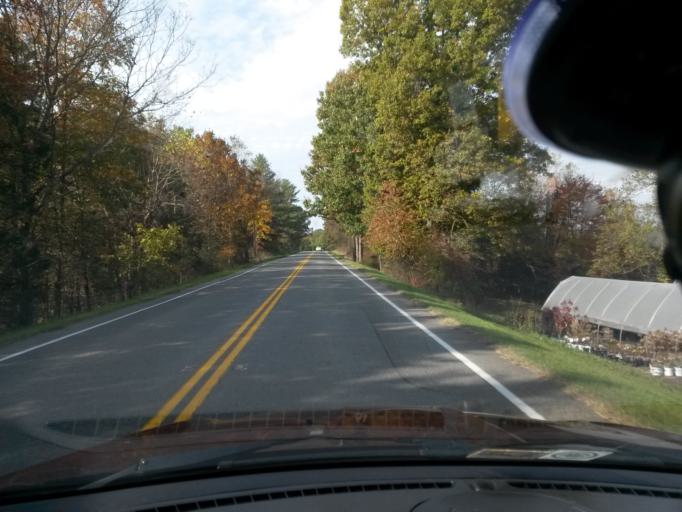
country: US
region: Virginia
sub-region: Franklin County
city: North Shore
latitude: 37.1179
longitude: -79.7947
